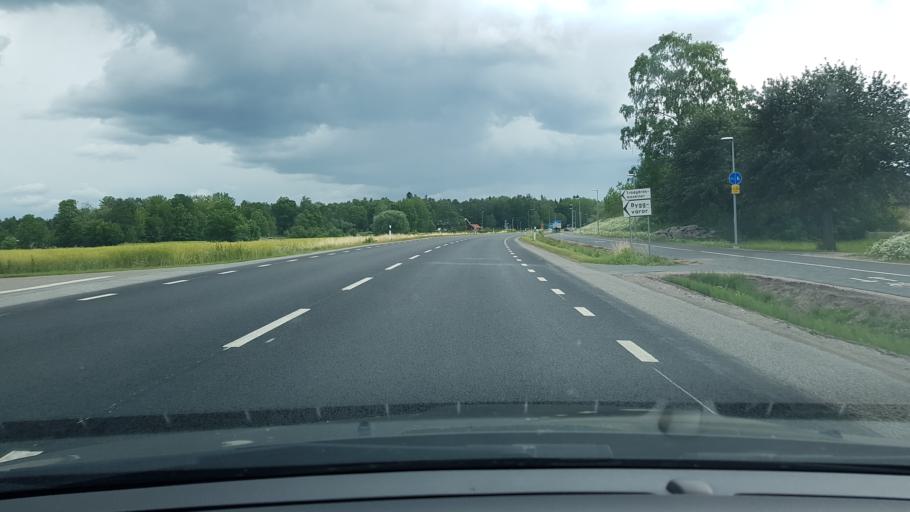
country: SE
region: Uppsala
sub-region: Uppsala Kommun
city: Saevja
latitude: 59.8239
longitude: 17.6982
